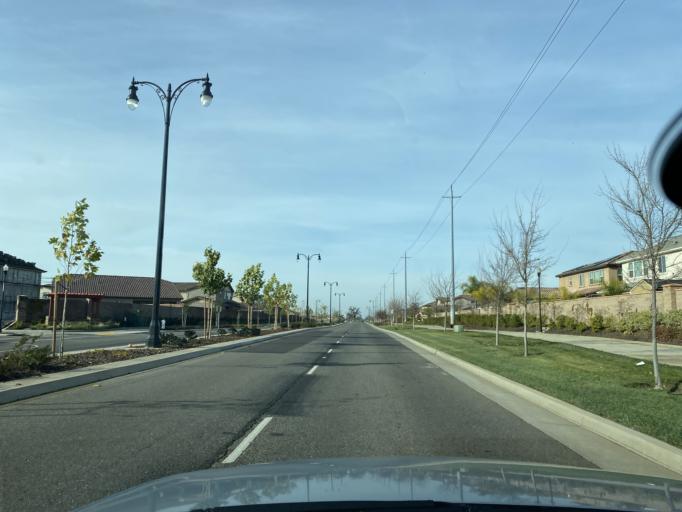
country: US
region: California
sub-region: Sacramento County
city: Elk Grove
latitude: 38.3945
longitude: -121.3845
